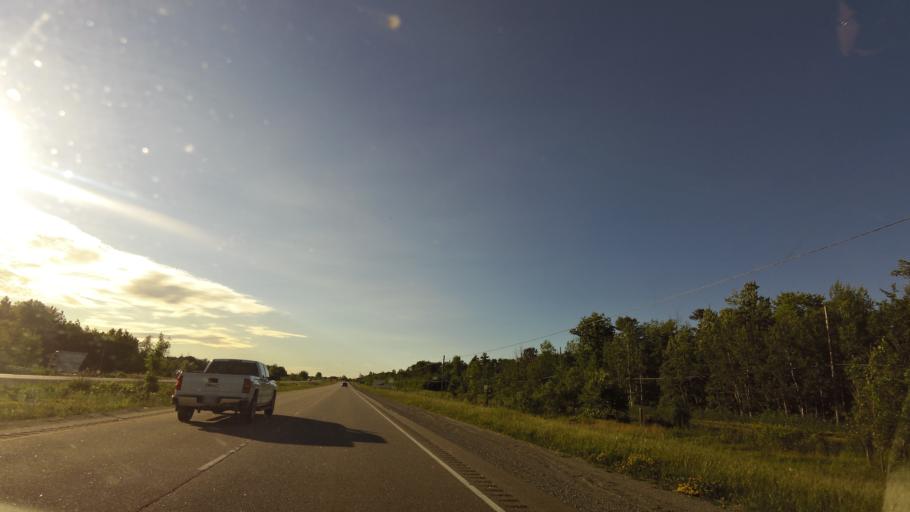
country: CA
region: Ontario
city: Midland
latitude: 44.7898
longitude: -79.7033
